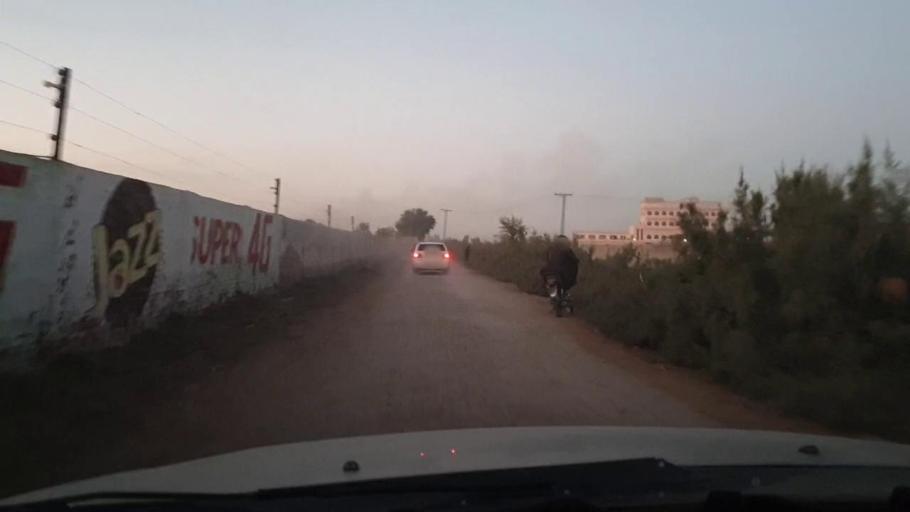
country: PK
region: Sindh
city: Ghotki
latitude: 27.9826
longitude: 69.2870
